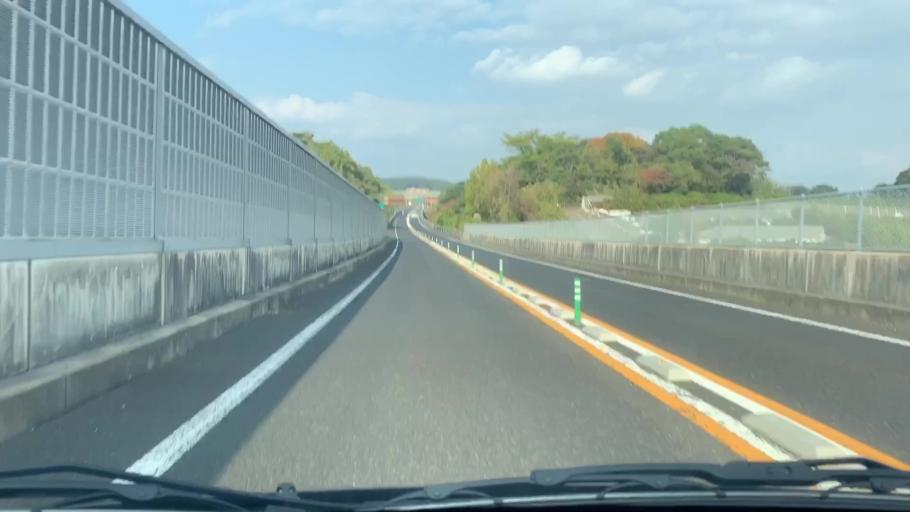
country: JP
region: Nagasaki
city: Sasebo
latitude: 33.0597
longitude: 129.7587
